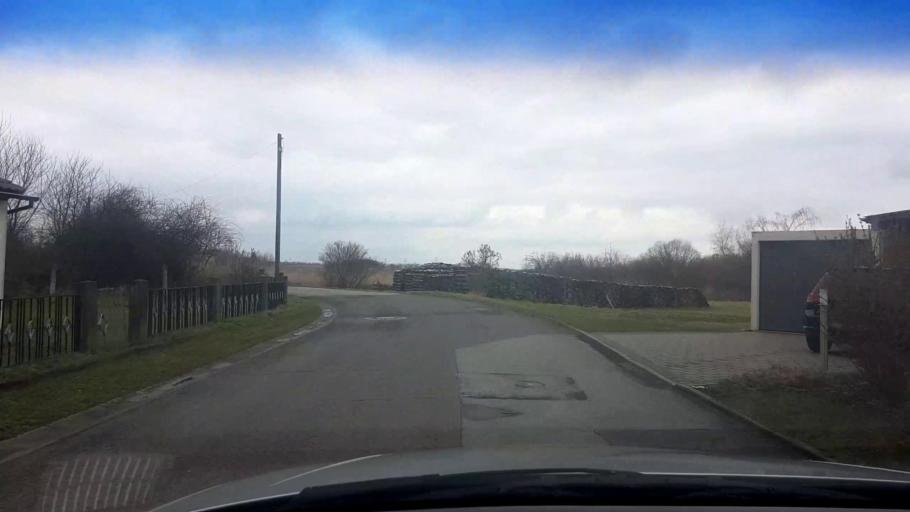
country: DE
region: Bavaria
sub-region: Regierungsbezirk Unterfranken
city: Knetzgau
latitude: 49.9696
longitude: 10.5624
